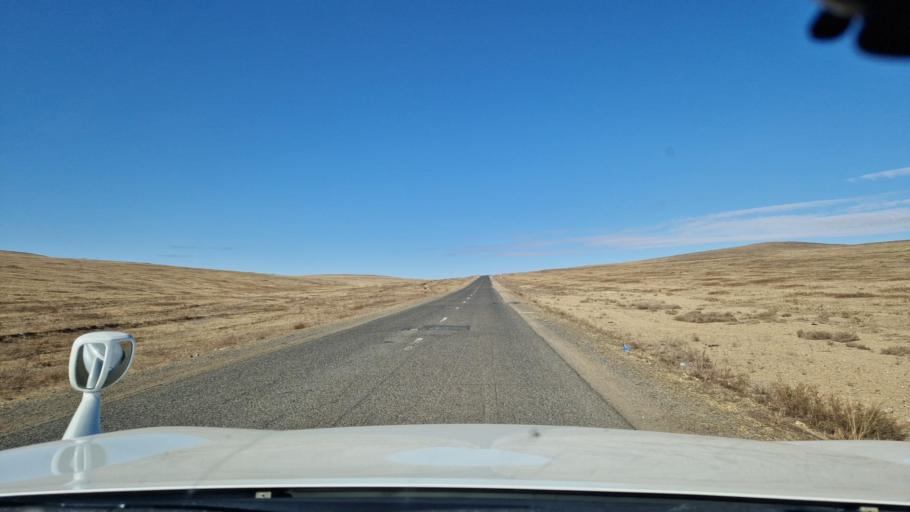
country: MN
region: Hentiy
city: Modot
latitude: 47.5470
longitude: 109.3810
